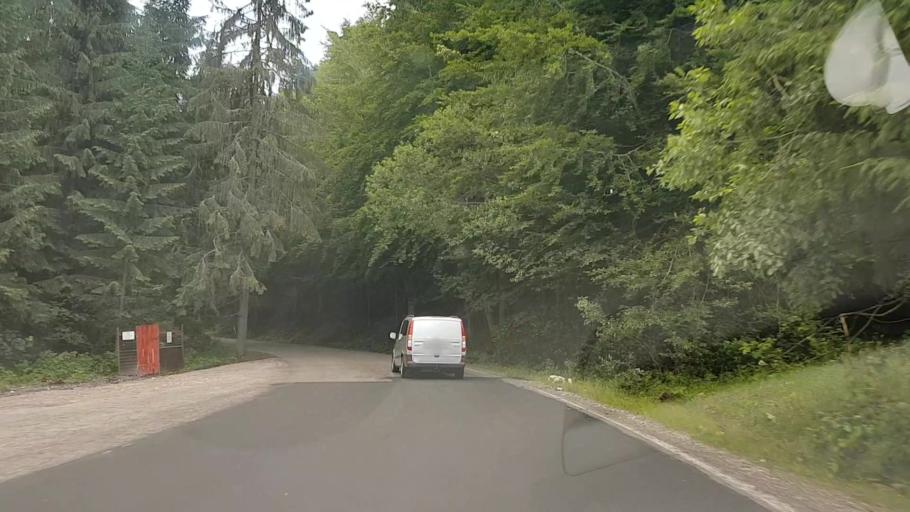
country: RO
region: Harghita
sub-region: Comuna Varsag
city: Varsag
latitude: 46.6643
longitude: 25.3184
